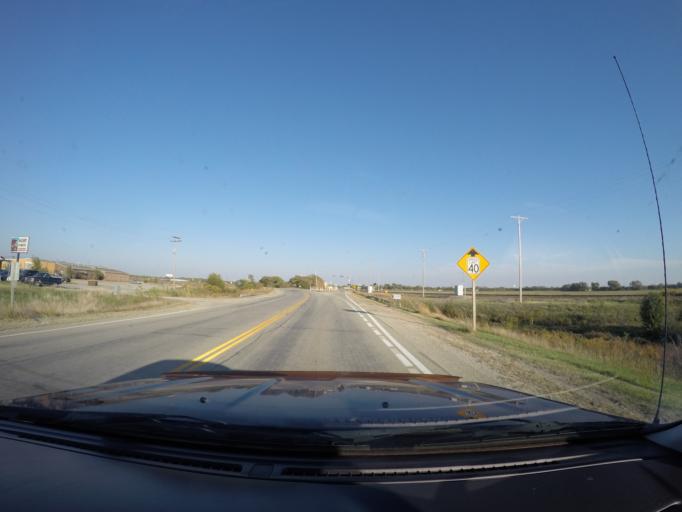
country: US
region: Kansas
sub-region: Saline County
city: Salina
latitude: 38.8417
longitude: -97.6388
